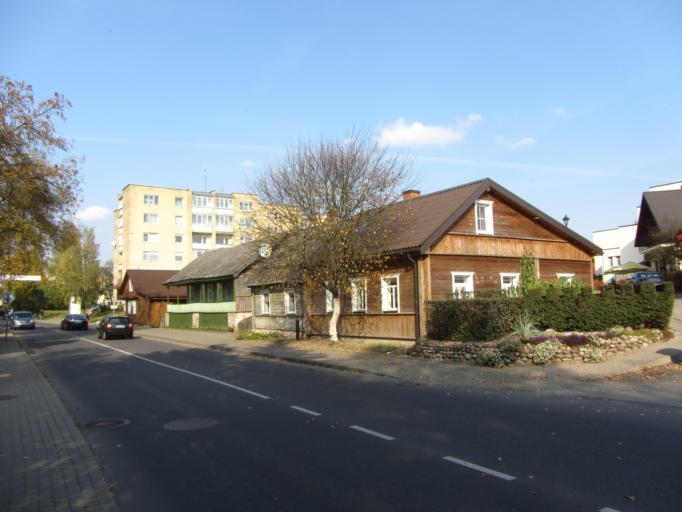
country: LT
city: Trakai
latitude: 54.6340
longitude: 24.9341
